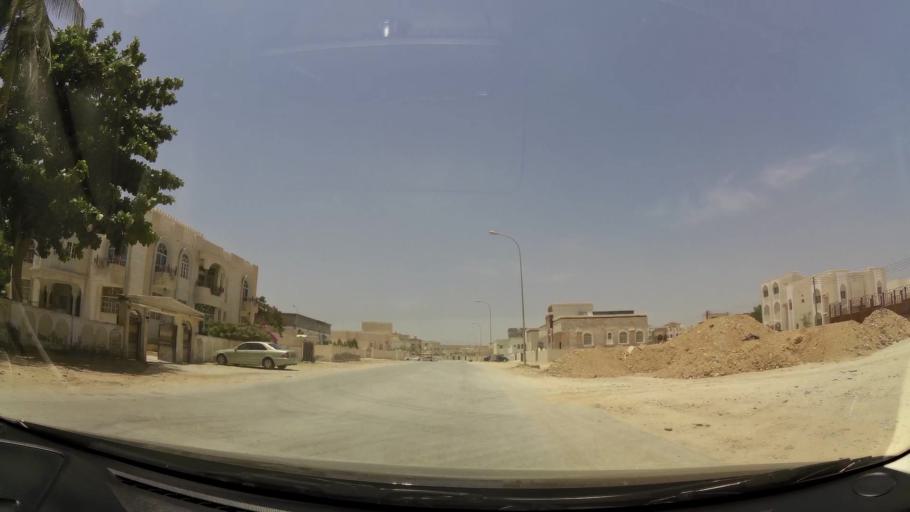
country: OM
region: Zufar
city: Salalah
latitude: 17.0693
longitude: 54.1554
